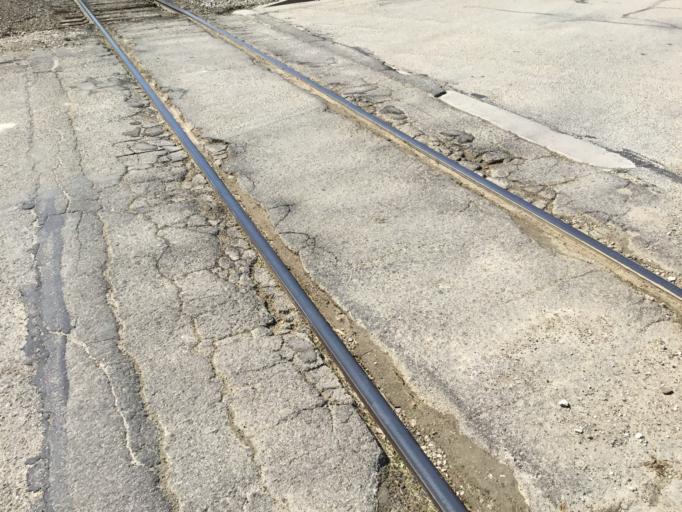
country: US
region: Kansas
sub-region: Mitchell County
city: Beloit
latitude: 39.4602
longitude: -98.1257
